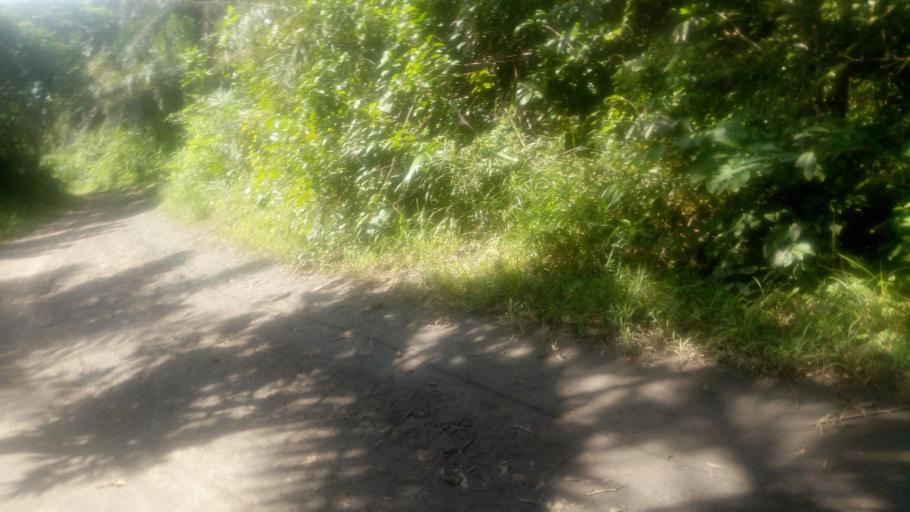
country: SL
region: Northern Province
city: Magburaka
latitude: 8.6594
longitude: -12.0691
